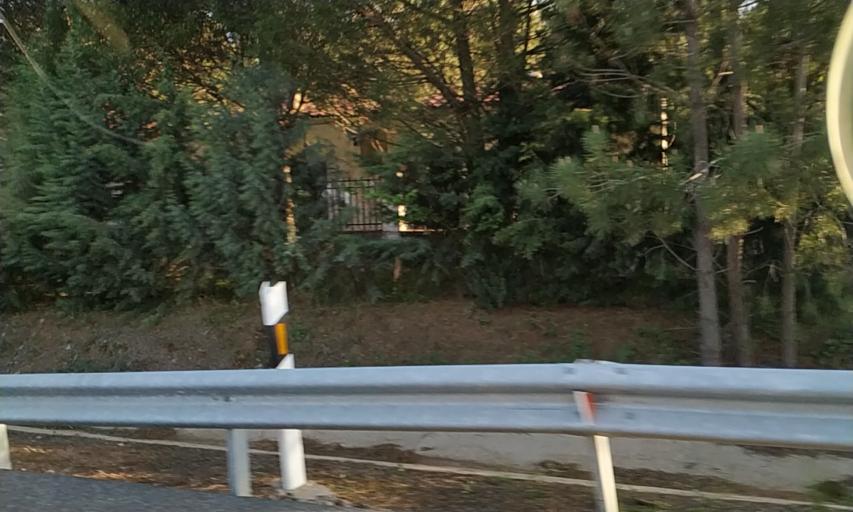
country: PT
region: Portalegre
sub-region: Portalegre
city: Sao Juliao
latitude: 39.3452
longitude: -7.2972
